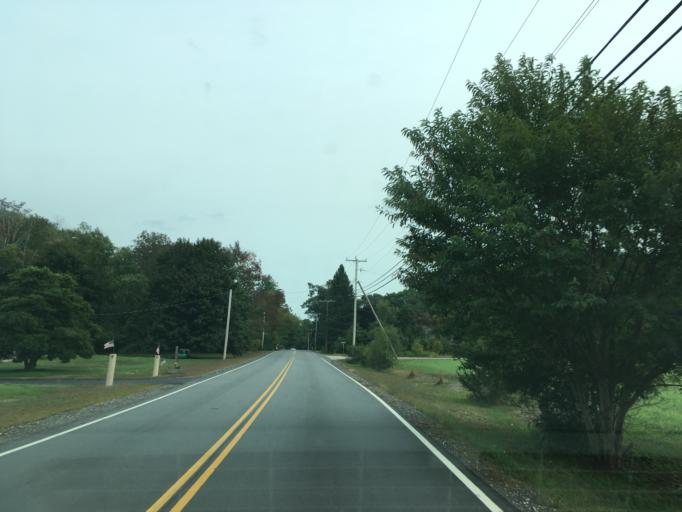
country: US
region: New Hampshire
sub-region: Rockingham County
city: Stratham Station
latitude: 43.0209
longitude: -70.8972
